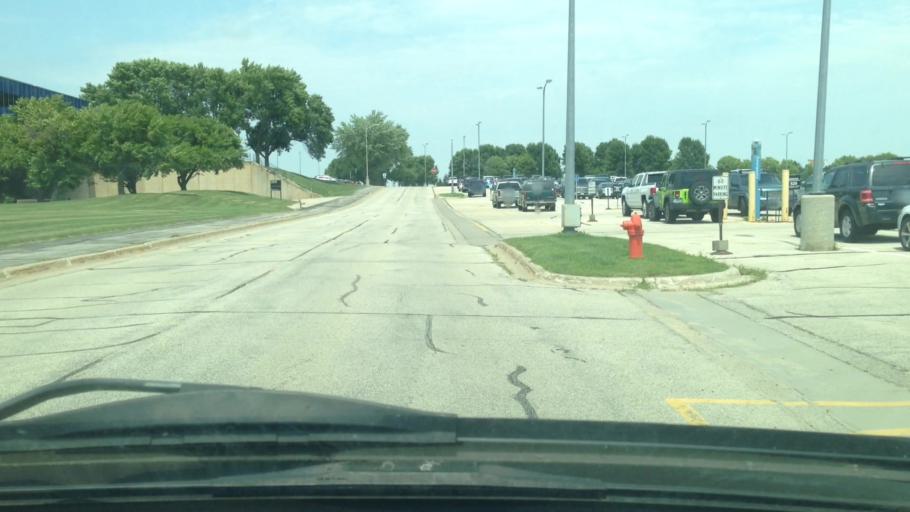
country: US
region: Minnesota
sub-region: Olmsted County
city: Rochester
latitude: 44.0582
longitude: -92.5017
